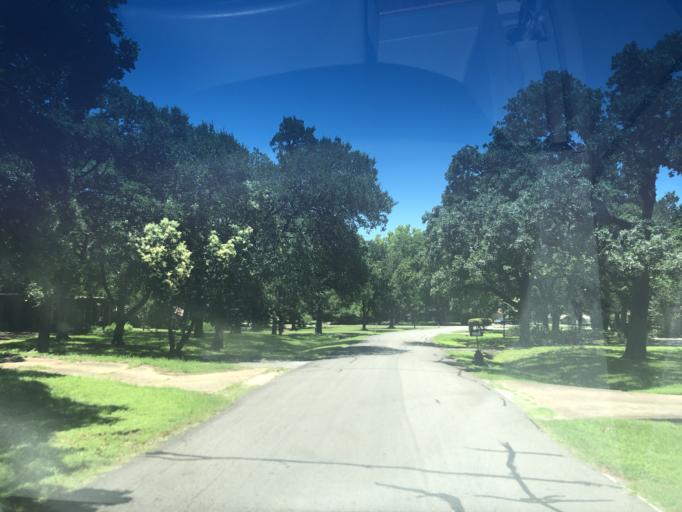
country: US
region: Texas
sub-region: Dallas County
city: Grand Prairie
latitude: 32.7774
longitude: -97.0332
